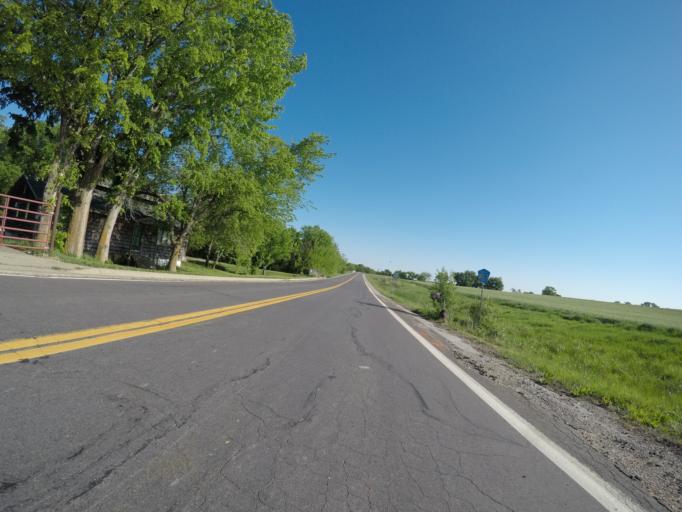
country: US
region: Kansas
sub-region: Shawnee County
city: Topeka
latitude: 39.0106
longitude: -95.4734
